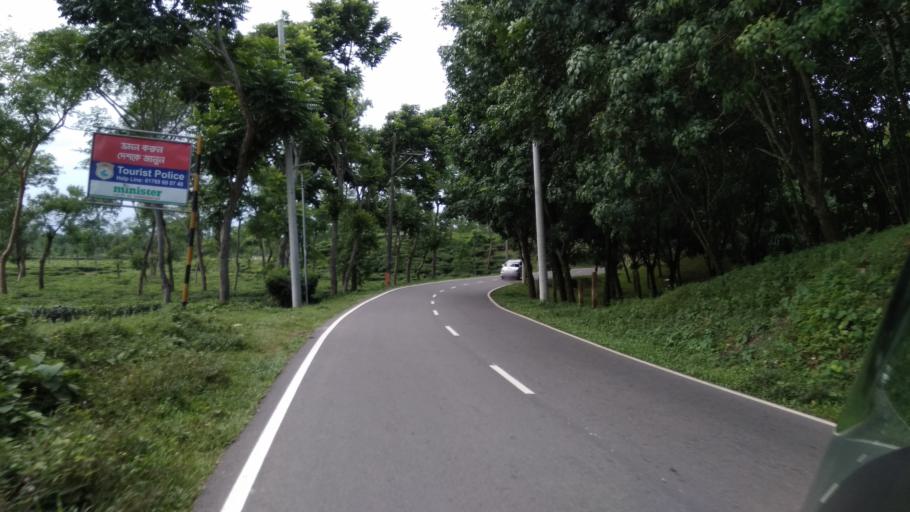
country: IN
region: Tripura
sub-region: Dhalai
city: Kamalpur
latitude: 24.3003
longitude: 91.7551
